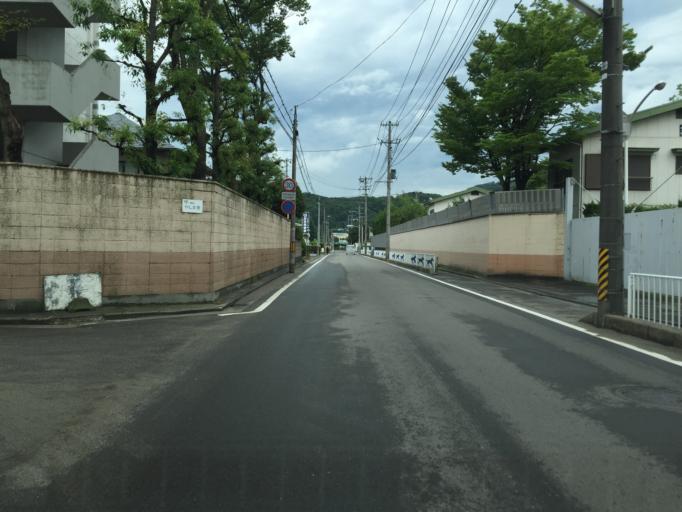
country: JP
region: Fukushima
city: Fukushima-shi
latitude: 37.7676
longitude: 140.4851
